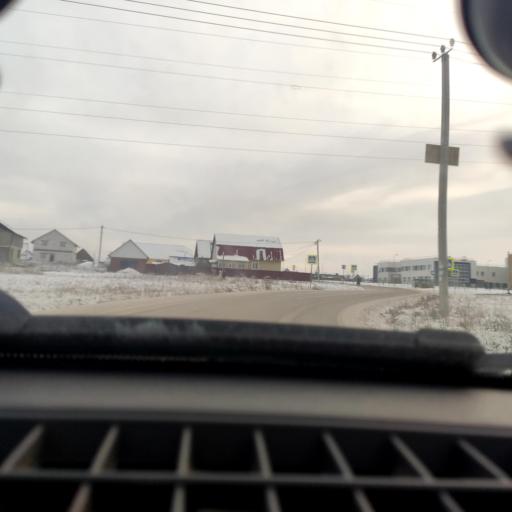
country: RU
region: Bashkortostan
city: Iglino
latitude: 54.8267
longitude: 56.4377
